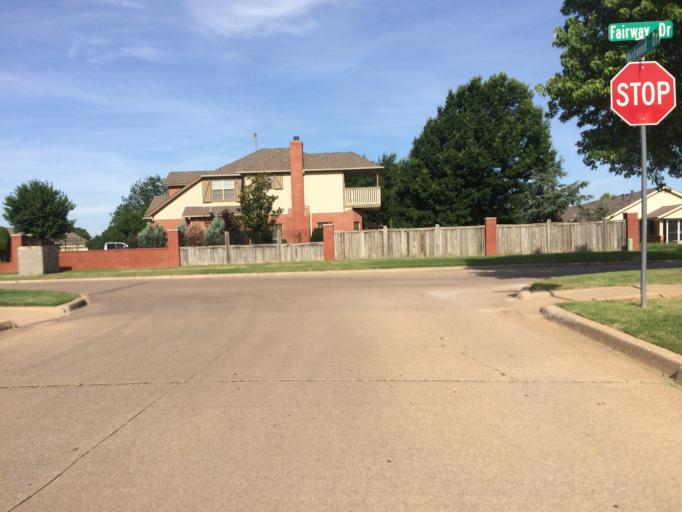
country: US
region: Oklahoma
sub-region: Cleveland County
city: Norman
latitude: 35.2277
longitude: -97.4763
